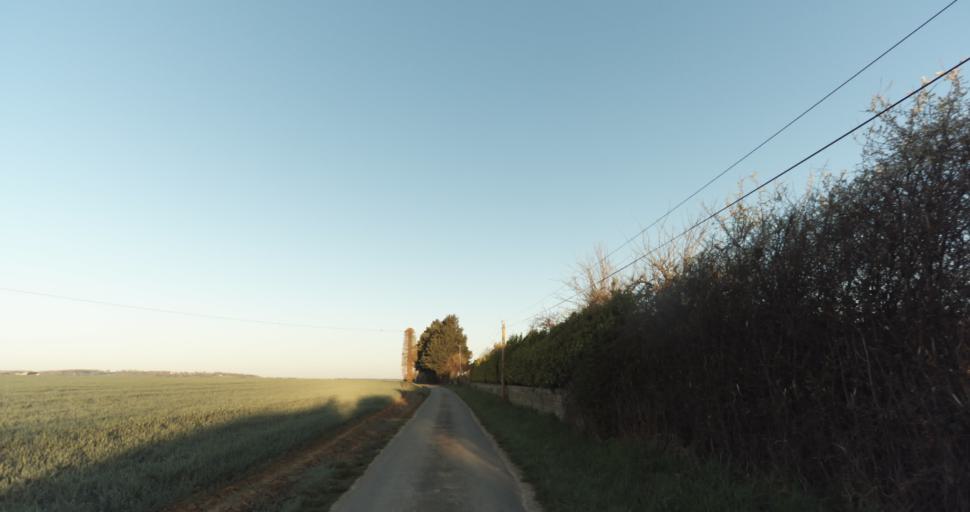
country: FR
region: Lower Normandy
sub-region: Departement du Calvados
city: Saint-Pierre-sur-Dives
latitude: 49.0381
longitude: -0.0400
